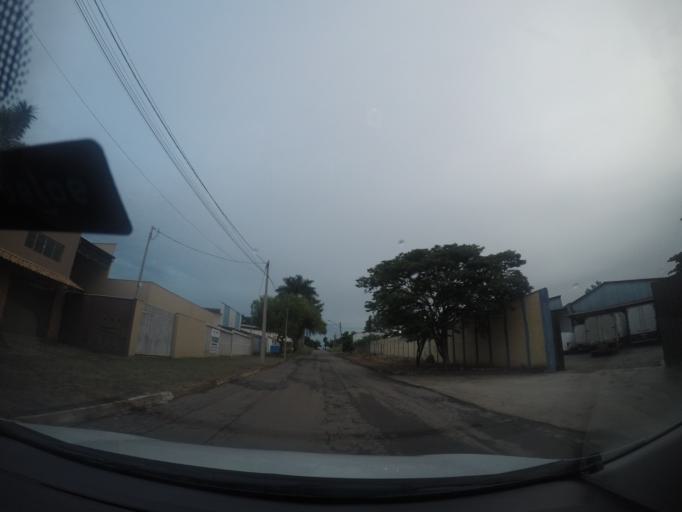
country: BR
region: Goias
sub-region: Goiania
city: Goiania
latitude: -16.6380
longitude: -49.2445
